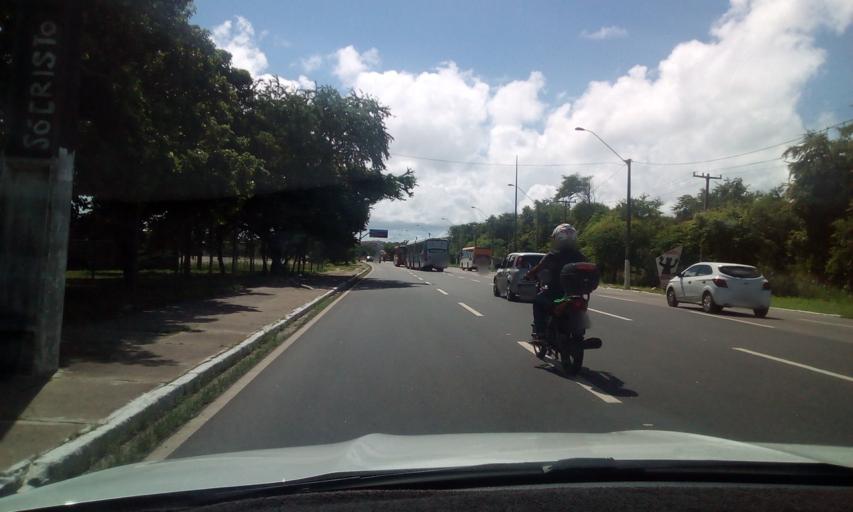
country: BR
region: Pernambuco
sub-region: Olinda
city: Olinda
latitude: -8.0325
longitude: -34.8663
